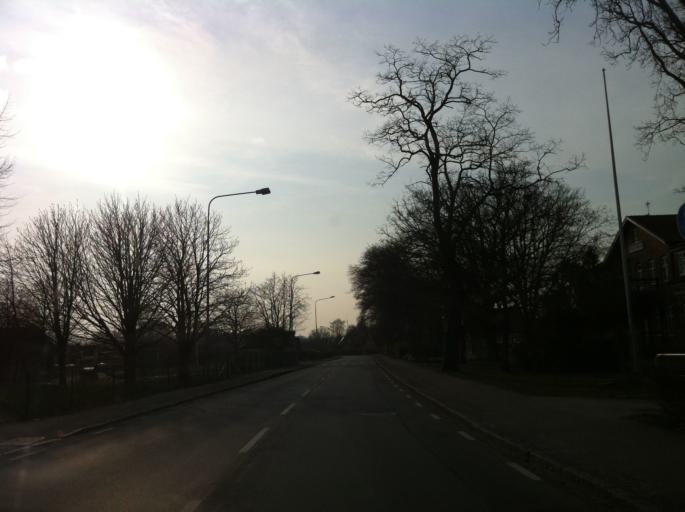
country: SE
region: Skane
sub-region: Svalovs Kommun
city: Svaloev
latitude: 55.9150
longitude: 13.1612
